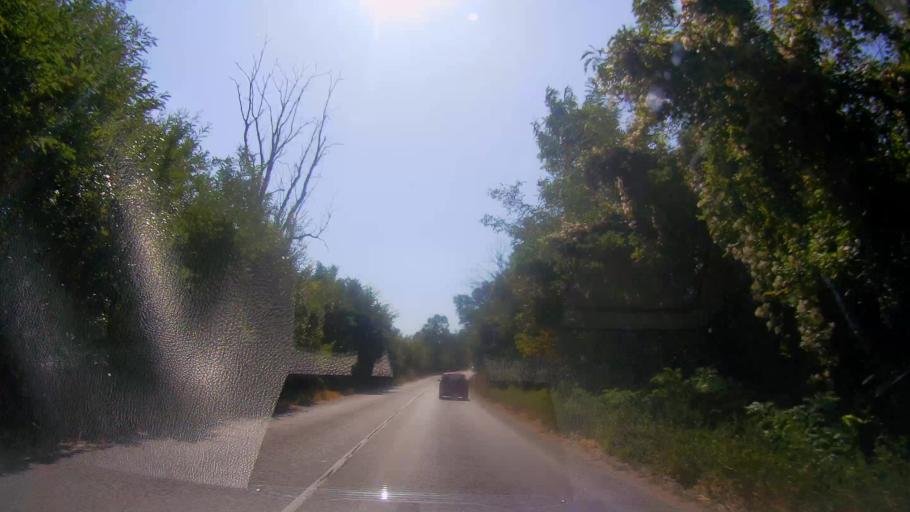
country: BG
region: Veliko Turnovo
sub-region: Obshtina Gorna Oryakhovitsa
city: Purvomaytsi
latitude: 43.2499
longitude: 25.6442
